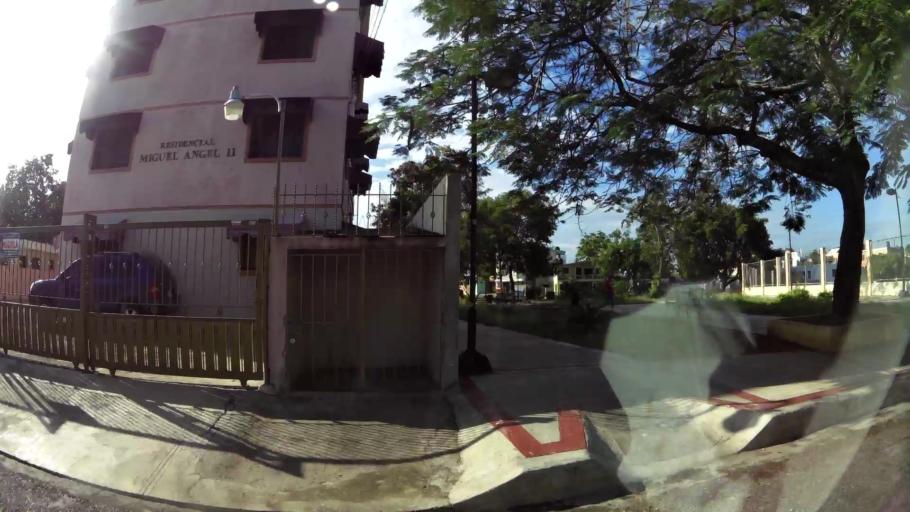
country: DO
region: Santo Domingo
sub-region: Santo Domingo
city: Santo Domingo Este
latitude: 18.4875
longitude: -69.8597
